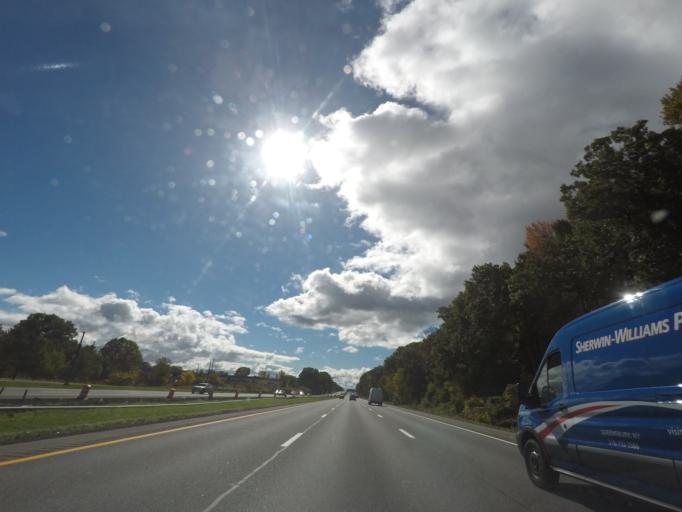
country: US
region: New York
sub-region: Saratoga County
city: Country Knolls
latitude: 42.8760
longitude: -73.7777
